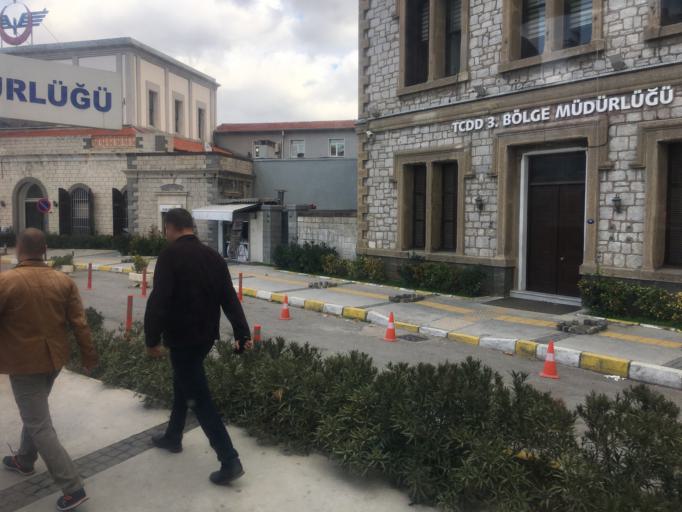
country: TR
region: Izmir
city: Izmir
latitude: 38.4381
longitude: 27.1477
